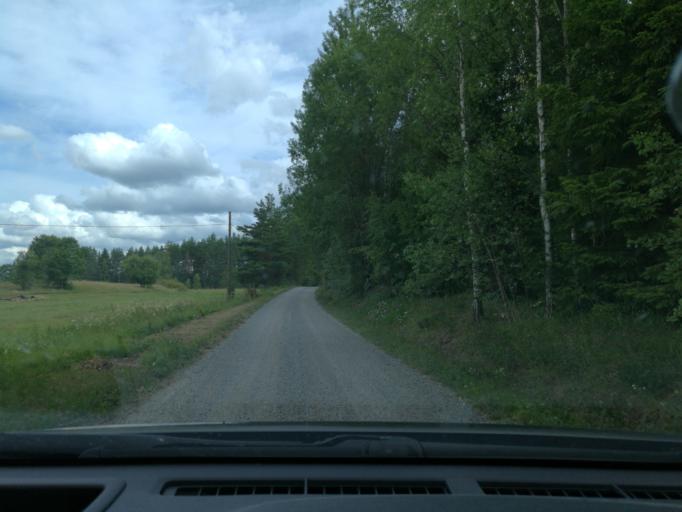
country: SE
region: Stockholm
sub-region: Sigtuna Kommun
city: Marsta
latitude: 59.6661
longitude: 17.9011
